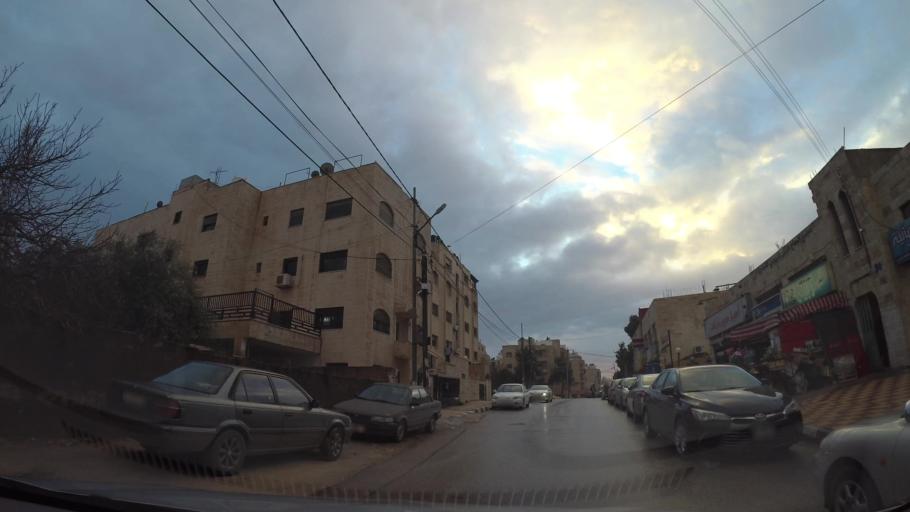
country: JO
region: Amman
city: Al Jubayhah
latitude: 32.0299
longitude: 35.8266
